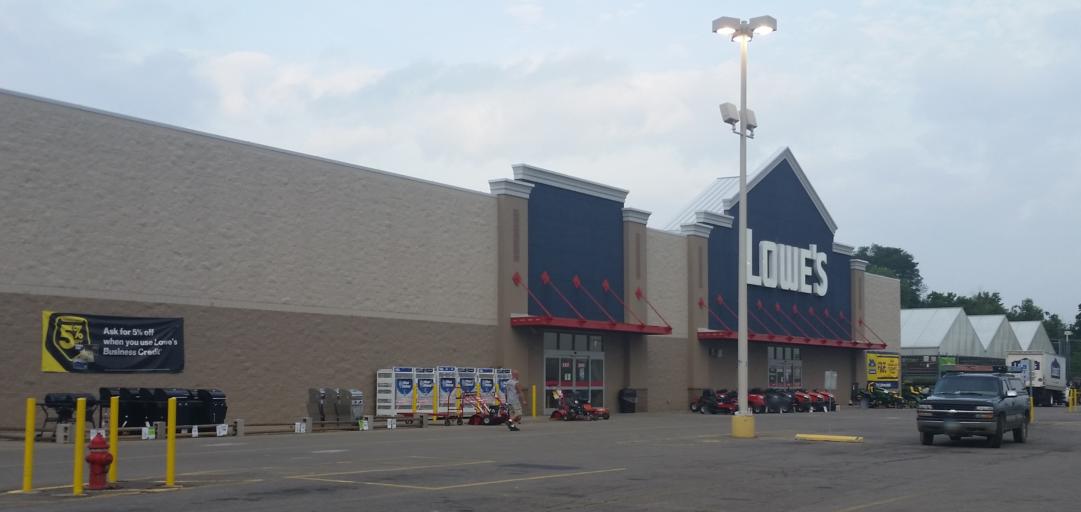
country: US
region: Ohio
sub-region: Knox County
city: Mount Vernon
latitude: 40.3993
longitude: -82.4507
